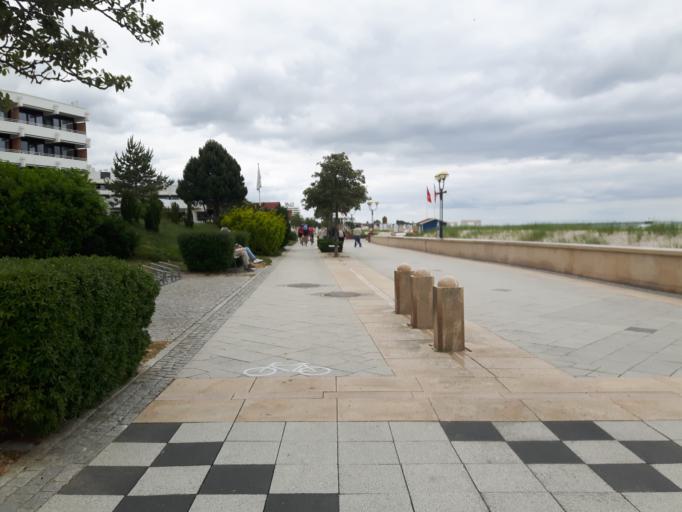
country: DE
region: Schleswig-Holstein
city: Gromitz
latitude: 54.1388
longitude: 10.9499
